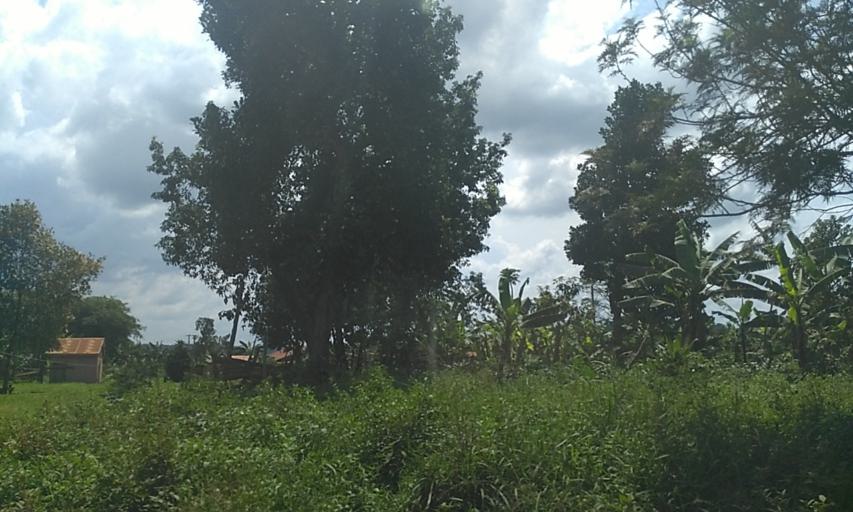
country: UG
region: Central Region
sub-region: Wakiso District
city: Wakiso
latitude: 0.3956
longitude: 32.4727
